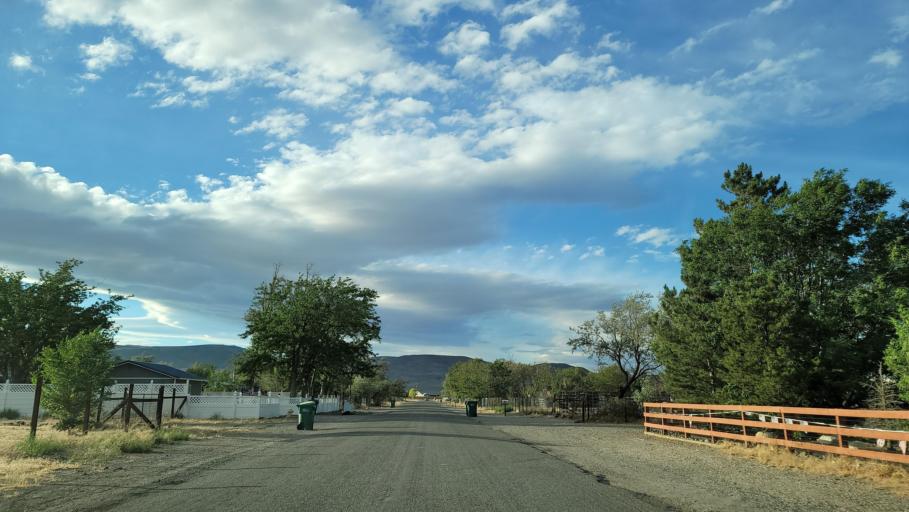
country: US
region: Nevada
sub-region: Lyon County
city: Silver Springs
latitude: 39.3962
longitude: -119.2374
